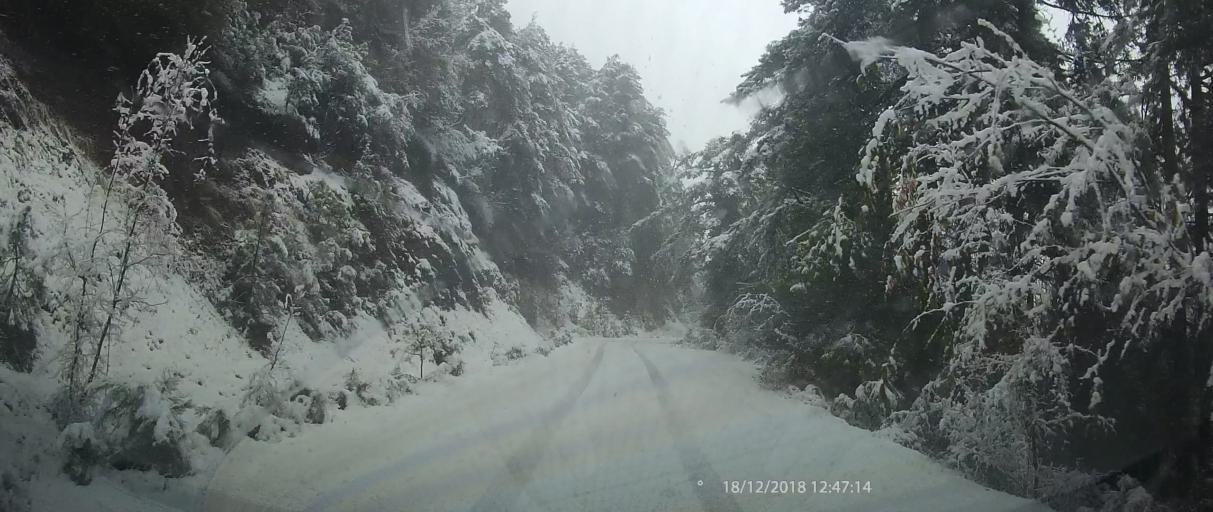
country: GR
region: Central Macedonia
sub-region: Nomos Pierias
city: Litochoro
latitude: 40.1001
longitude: 22.4358
